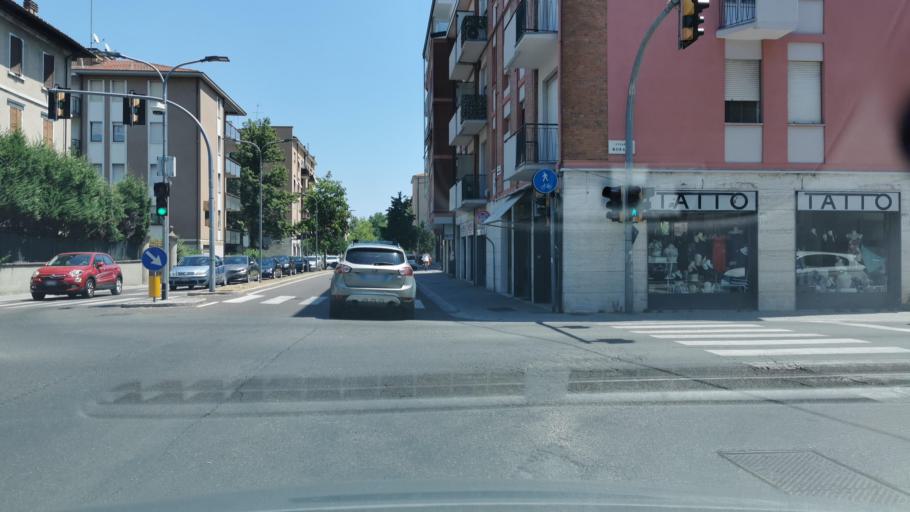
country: IT
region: Emilia-Romagna
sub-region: Provincia di Modena
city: Modena
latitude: 44.6344
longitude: 10.9261
